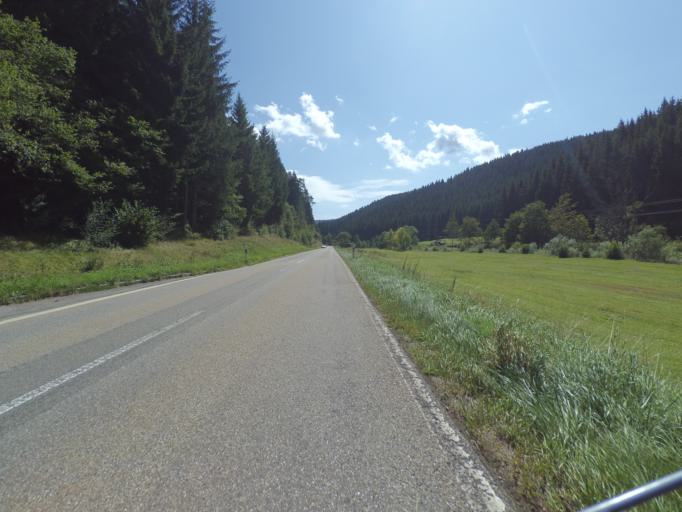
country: DE
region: Baden-Wuerttemberg
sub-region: Freiburg Region
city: Vohrenbach
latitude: 48.0133
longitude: 8.3205
